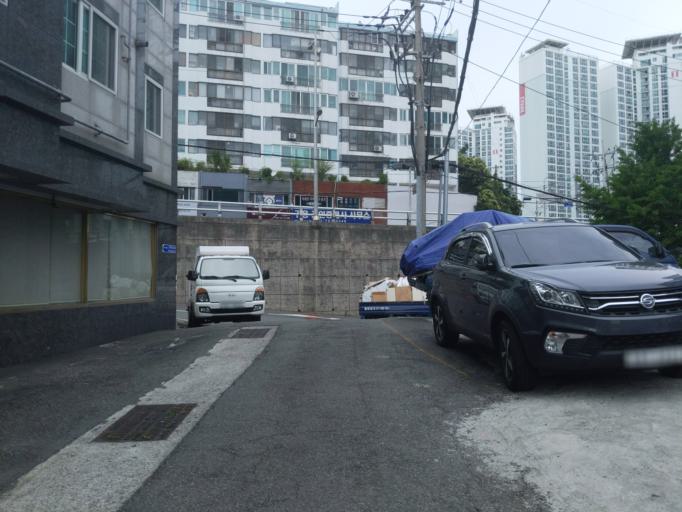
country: KR
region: Busan
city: Busan
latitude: 35.1599
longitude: 129.1290
